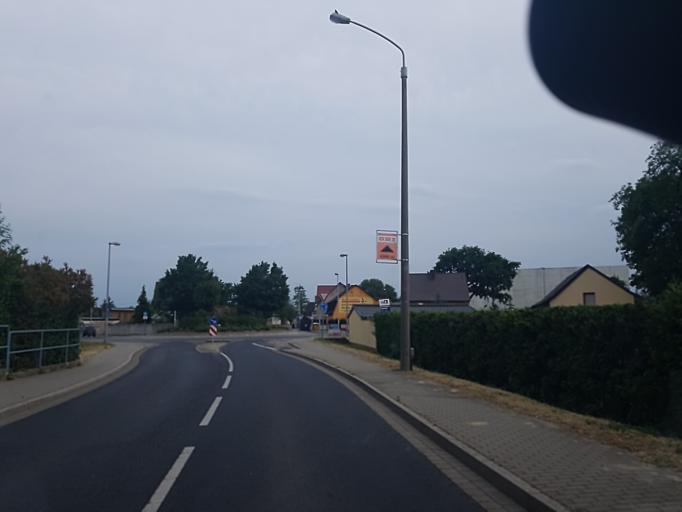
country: DE
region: Saxony-Anhalt
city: Wittenburg
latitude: 51.8791
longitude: 12.6315
